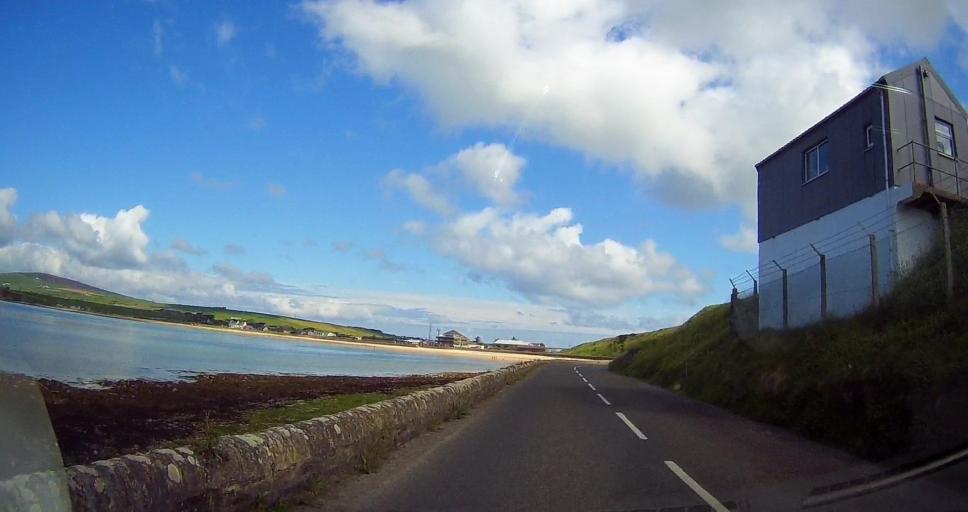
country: GB
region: Scotland
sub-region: Orkney Islands
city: Orkney
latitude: 58.9568
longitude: -2.9696
